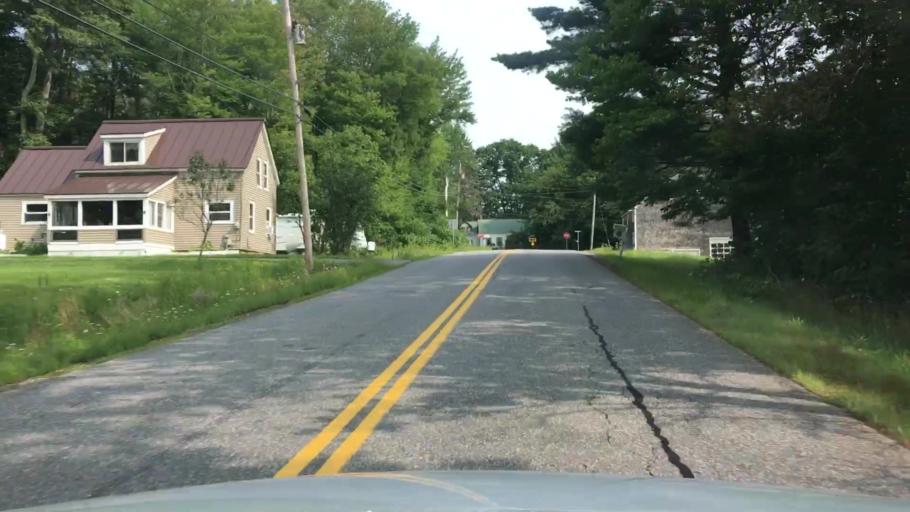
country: US
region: Maine
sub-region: Kennebec County
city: Chelsea
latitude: 44.3116
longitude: -69.6946
